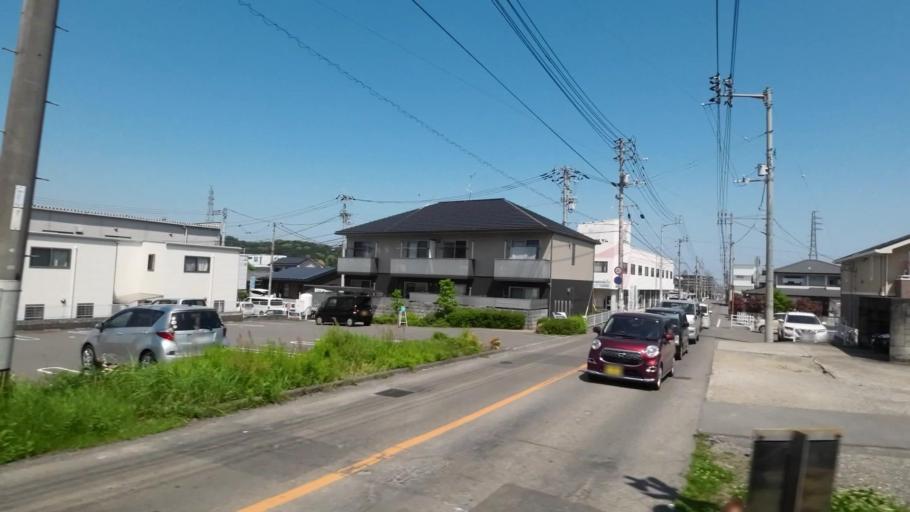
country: JP
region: Ehime
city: Niihama
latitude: 33.9432
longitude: 133.2892
